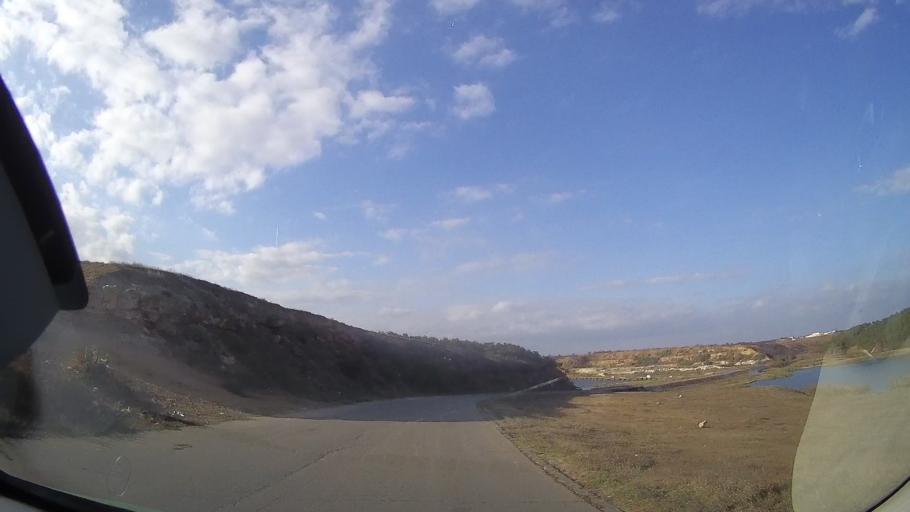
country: RO
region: Constanta
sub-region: Comuna Limanu
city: Limanu
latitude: 43.8105
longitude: 28.5181
